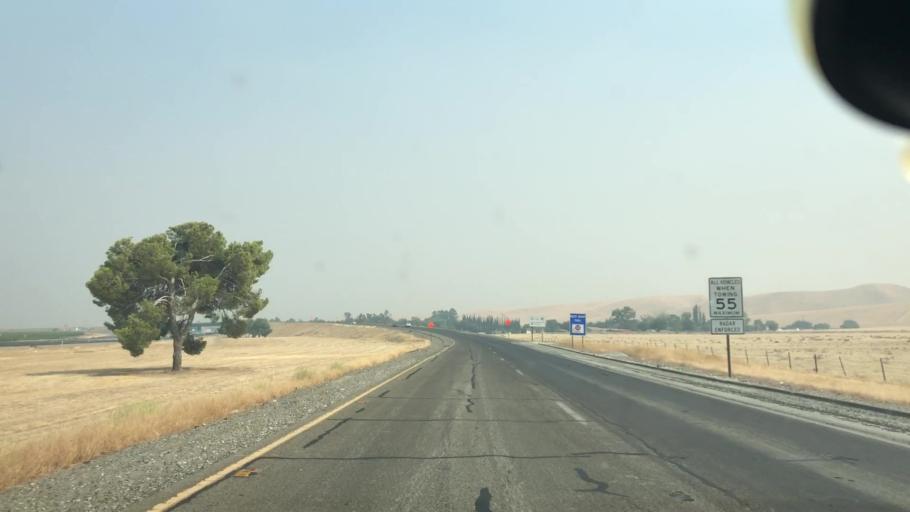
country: US
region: California
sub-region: San Joaquin County
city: Tracy
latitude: 37.6427
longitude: -121.4098
